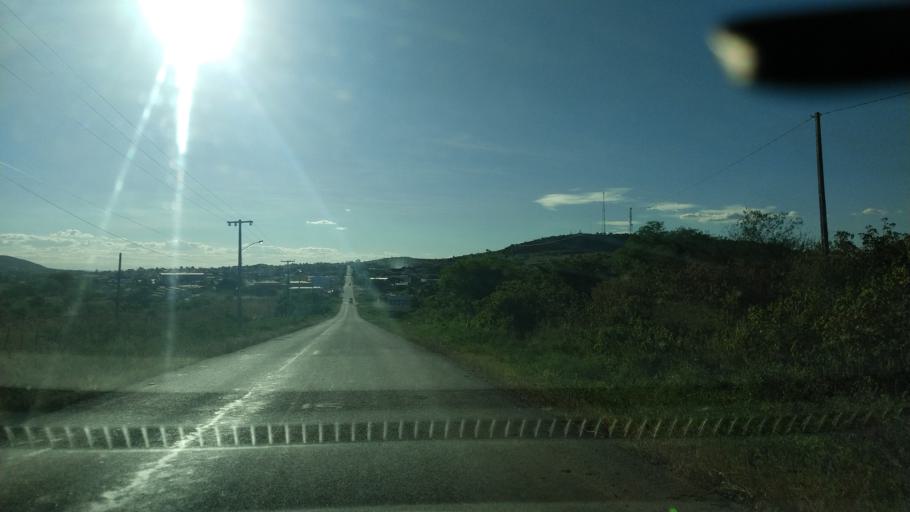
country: BR
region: Rio Grande do Norte
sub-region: Sao Jose Do Campestre
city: Sao Jose do Campestre
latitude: -6.3231
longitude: -35.7023
